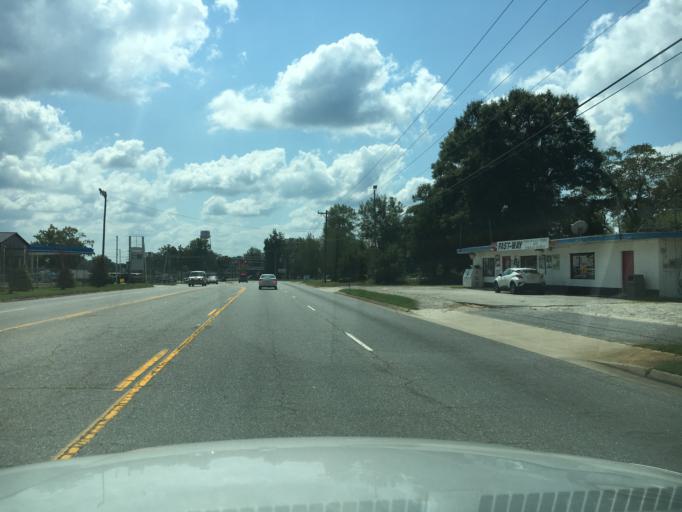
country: US
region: South Carolina
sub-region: Anderson County
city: Williamston
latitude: 34.6302
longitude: -82.3913
